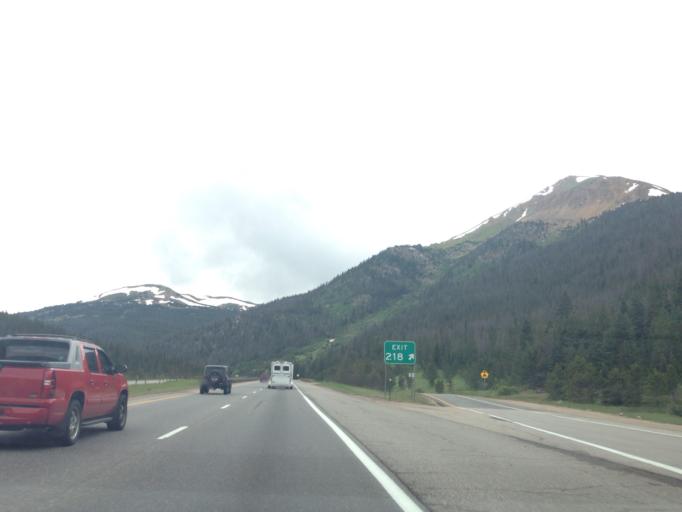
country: US
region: Colorado
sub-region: Clear Creek County
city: Georgetown
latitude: 39.7019
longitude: -105.8546
